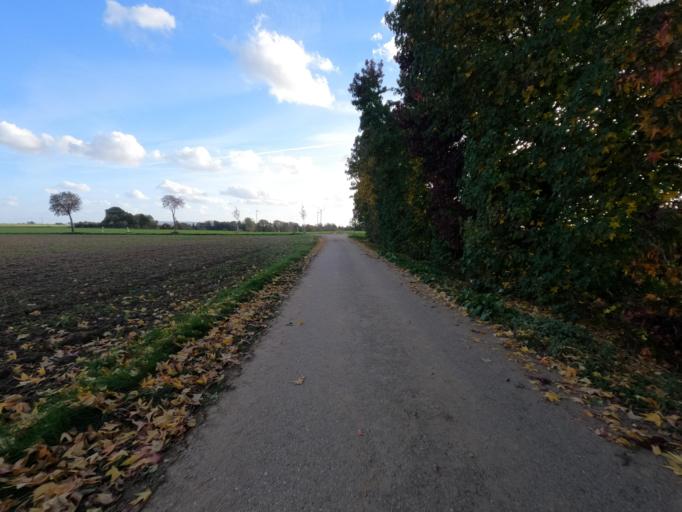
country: DE
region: North Rhine-Westphalia
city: Erkelenz
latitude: 51.0348
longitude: 6.3432
